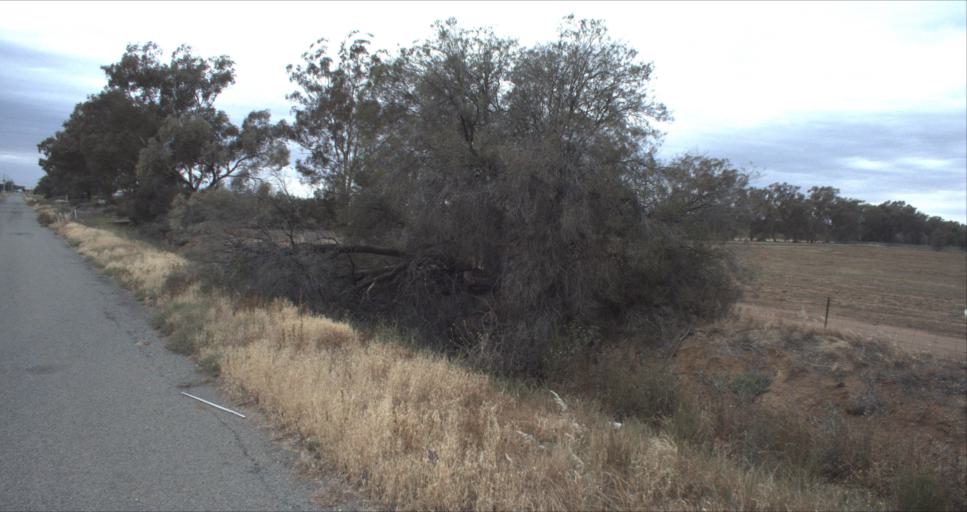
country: AU
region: New South Wales
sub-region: Leeton
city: Leeton
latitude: -34.5424
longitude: 146.3782
